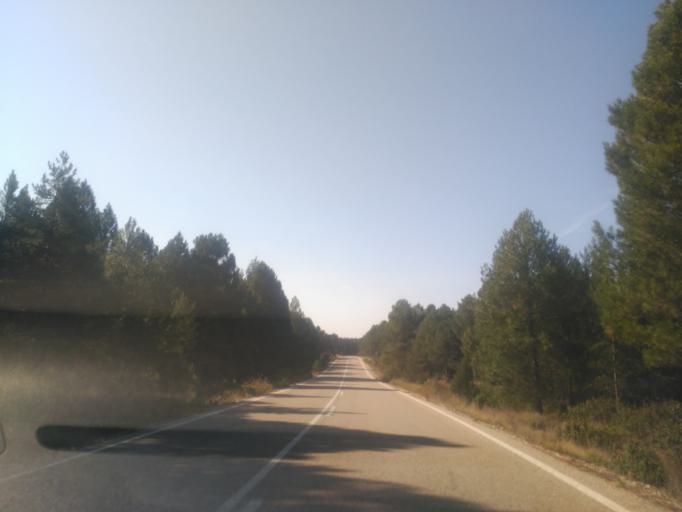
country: ES
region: Castille and Leon
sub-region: Provincia de Soria
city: Herrera de Soria
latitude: 41.7646
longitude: -3.0329
